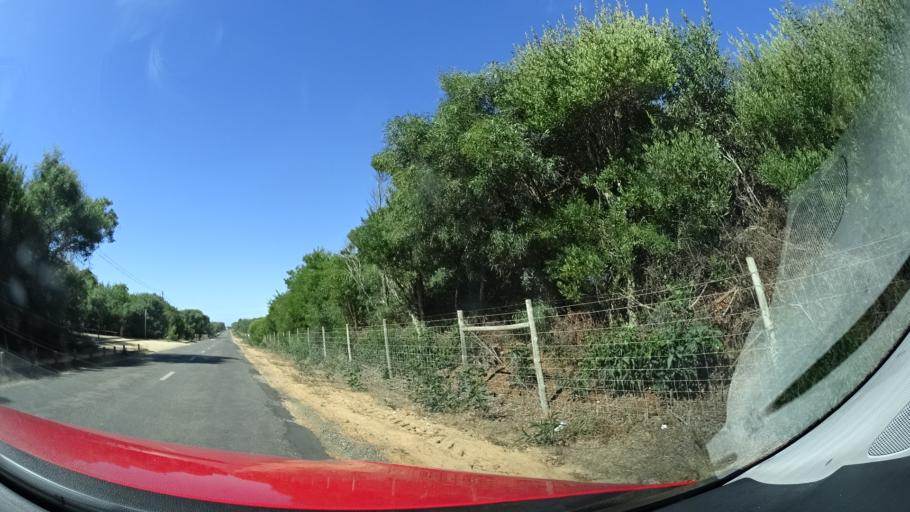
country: PT
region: Beja
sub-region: Odemira
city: Sao Teotonio
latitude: 37.5369
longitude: -8.7851
